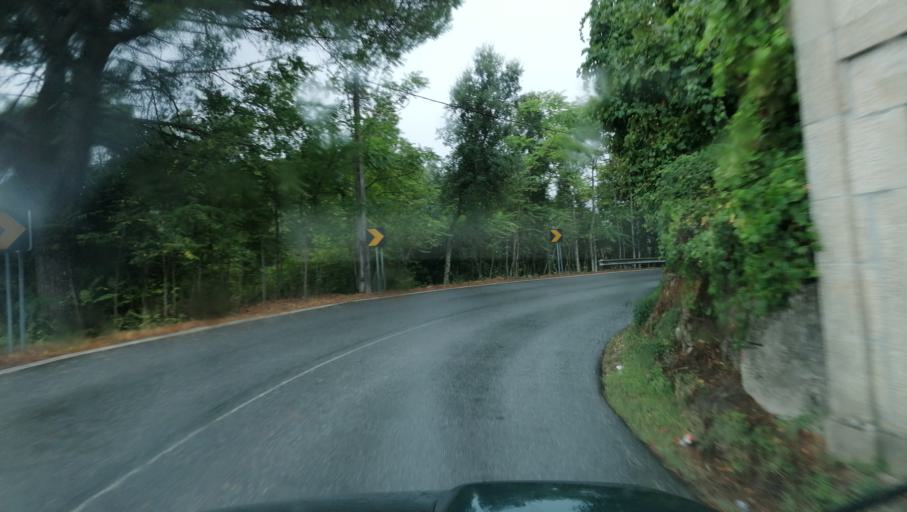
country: PT
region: Braga
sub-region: Cabeceiras de Basto
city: Cabeceiras de Basto
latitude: 41.4890
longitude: -7.9511
